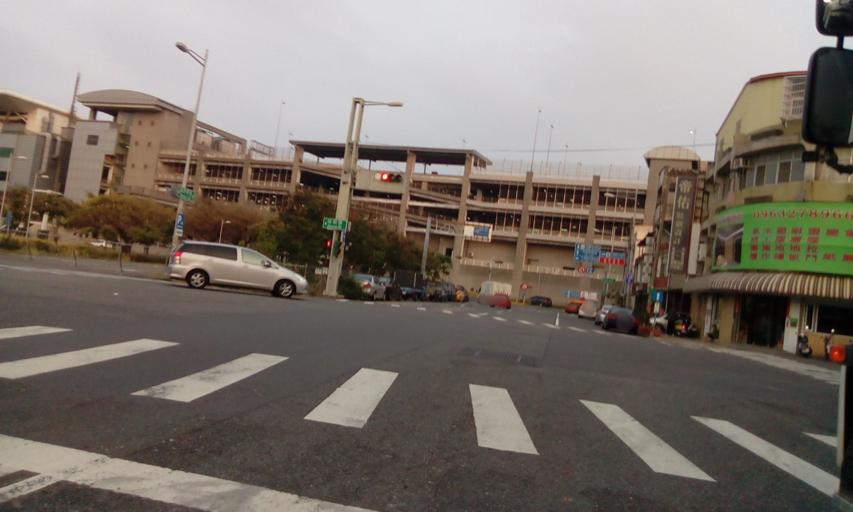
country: TW
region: Kaohsiung
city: Kaohsiung
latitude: 22.6872
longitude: 120.3046
